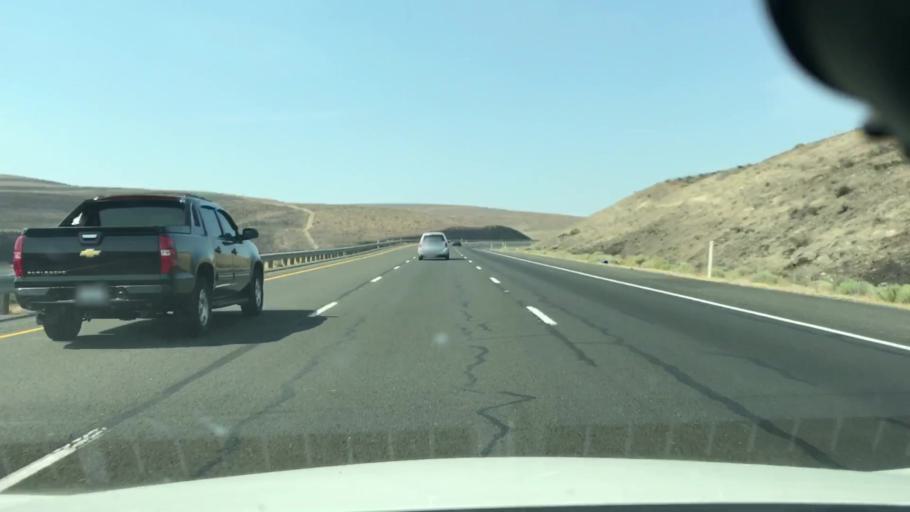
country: US
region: Washington
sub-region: Grant County
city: Mattawa
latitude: 46.9376
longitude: -120.0403
